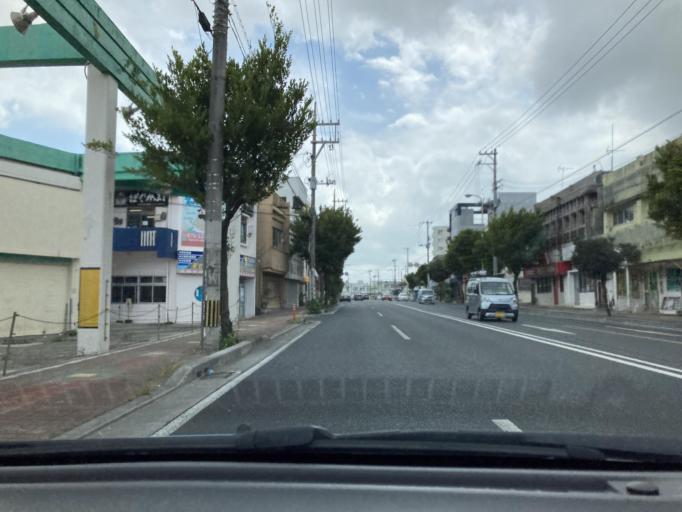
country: JP
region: Okinawa
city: Okinawa
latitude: 26.3367
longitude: 127.8171
